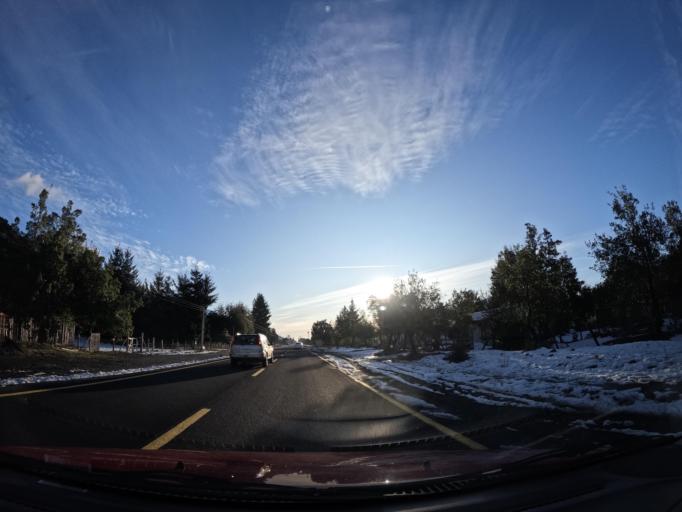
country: CL
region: Biobio
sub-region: Provincia de Nuble
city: Coihueco
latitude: -37.3616
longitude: -71.5243
